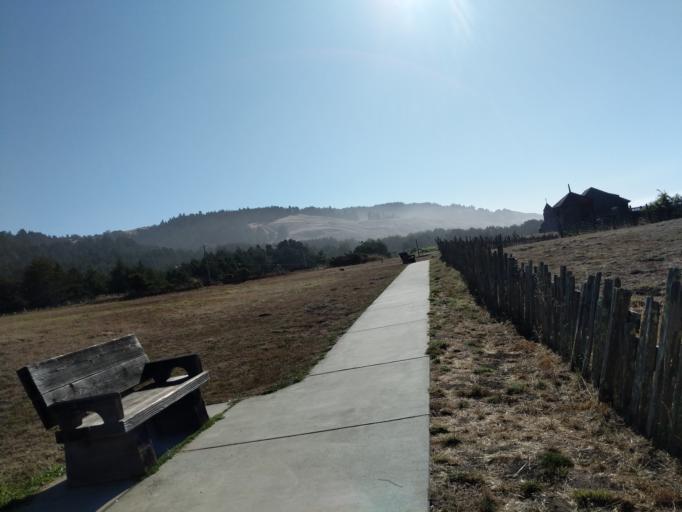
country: US
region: California
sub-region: Sonoma County
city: Monte Rio
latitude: 38.5154
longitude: -123.2448
